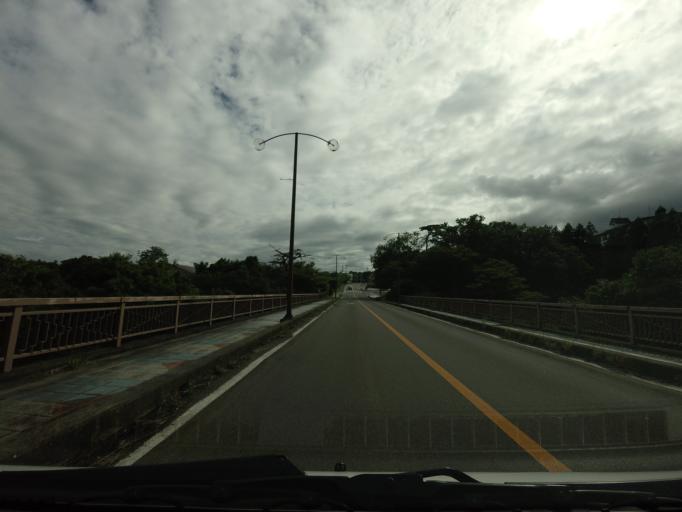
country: JP
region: Fukushima
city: Nihommatsu
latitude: 37.6075
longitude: 140.3588
